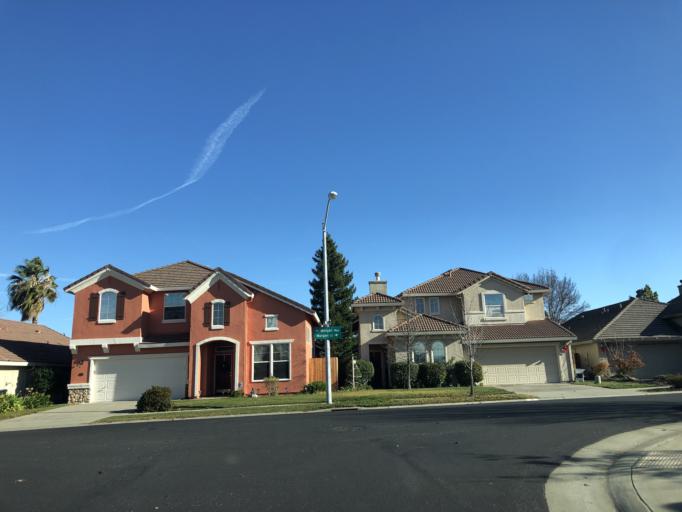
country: US
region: California
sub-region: Placer County
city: Roseville
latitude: 38.7813
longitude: -121.2917
